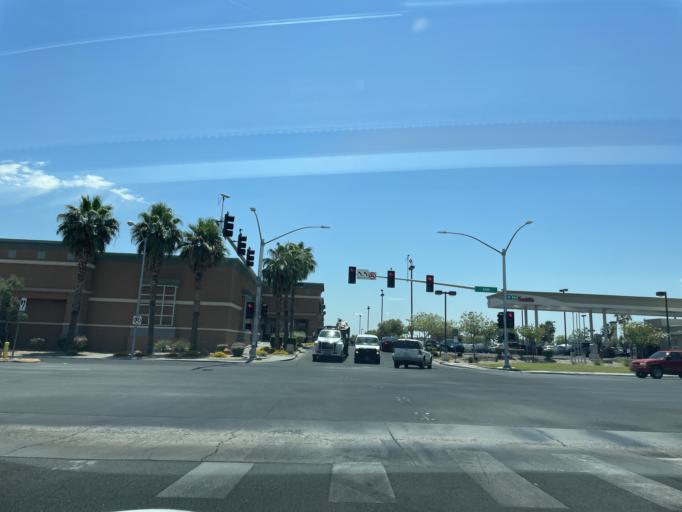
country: US
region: Nevada
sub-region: Clark County
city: North Las Vegas
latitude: 36.2620
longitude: -115.1543
